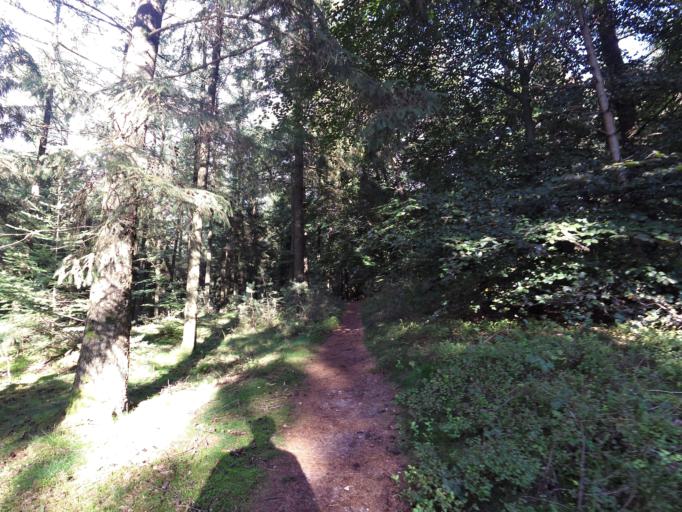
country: NL
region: Gelderland
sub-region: Gemeente Montferland
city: s-Heerenberg
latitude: 51.9187
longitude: 6.2430
